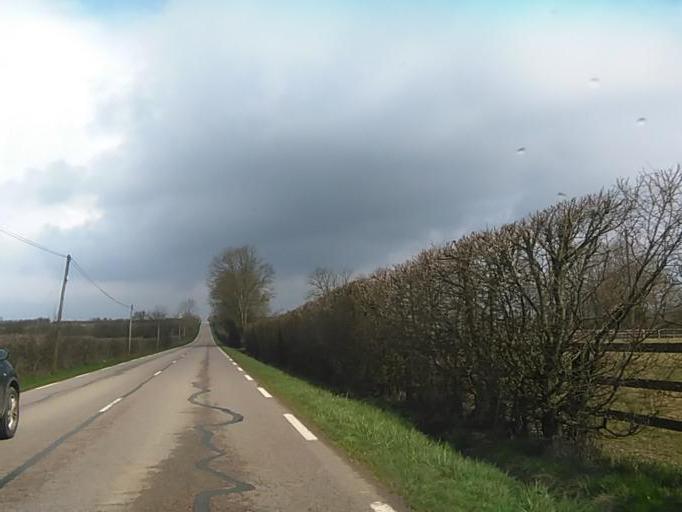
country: FR
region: Lower Normandy
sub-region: Departement de l'Orne
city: Pont-Ecrepin
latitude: 48.8042
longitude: -0.2431
